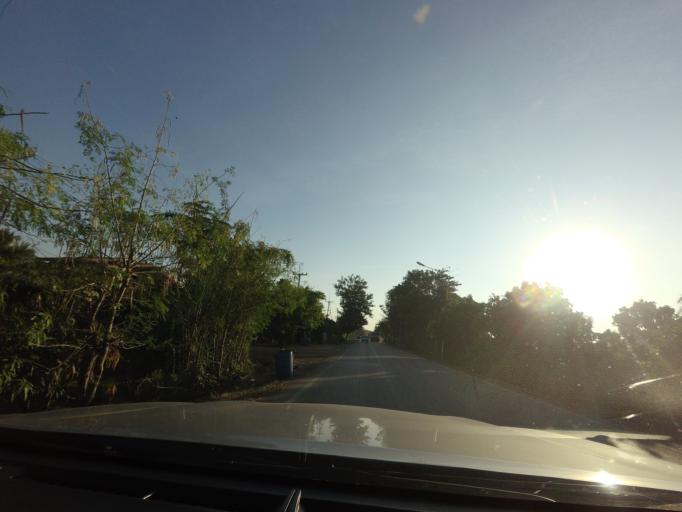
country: TH
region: Sukhothai
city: Sawankhalok
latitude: 17.3868
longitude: 99.7926
